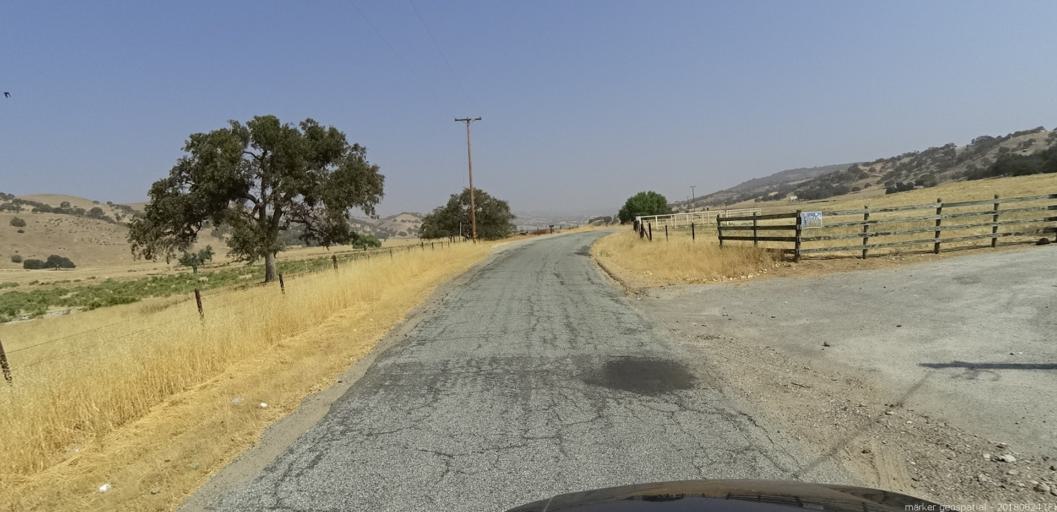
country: US
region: California
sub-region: San Luis Obispo County
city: San Miguel
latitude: 35.8820
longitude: -120.7022
